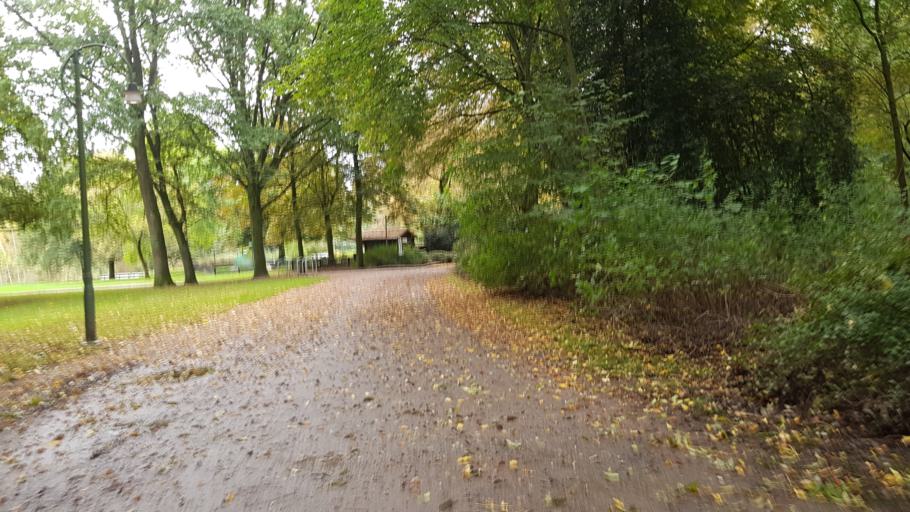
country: DE
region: Bremen
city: Bremen
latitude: 53.0934
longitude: 8.8221
